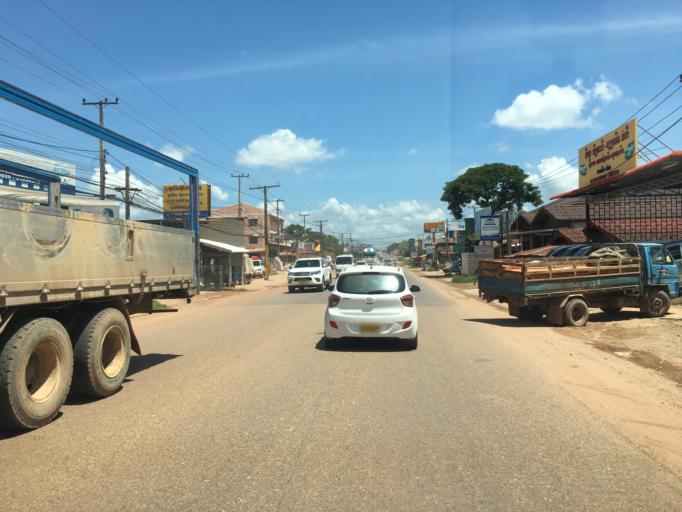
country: TH
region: Nong Khai
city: Si Chiang Mai
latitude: 18.0058
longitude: 102.5448
